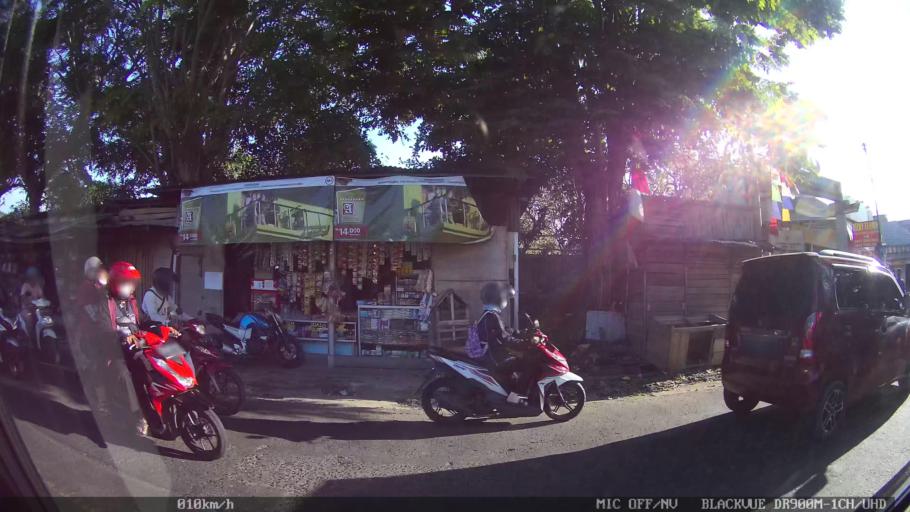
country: ID
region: Lampung
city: Kedaton
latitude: -5.3928
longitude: 105.2286
